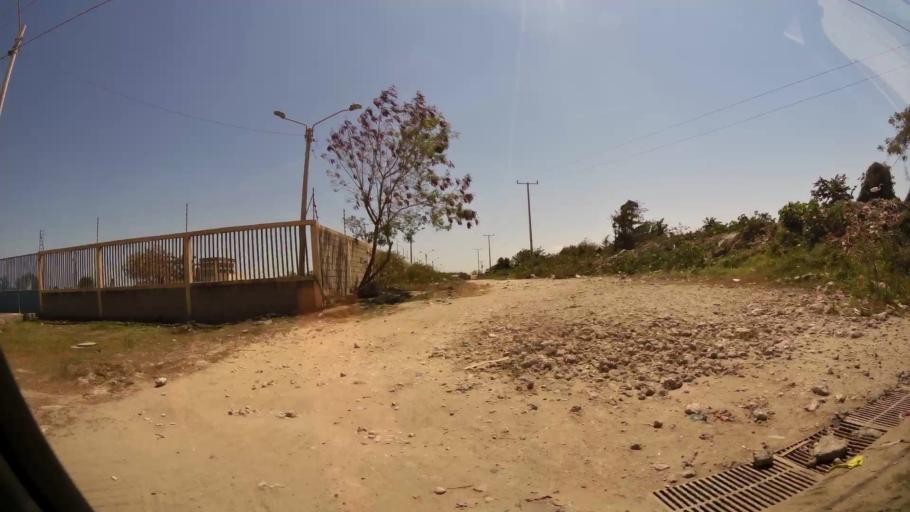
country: CO
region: Atlantico
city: Barranquilla
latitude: 10.9800
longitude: -74.7677
